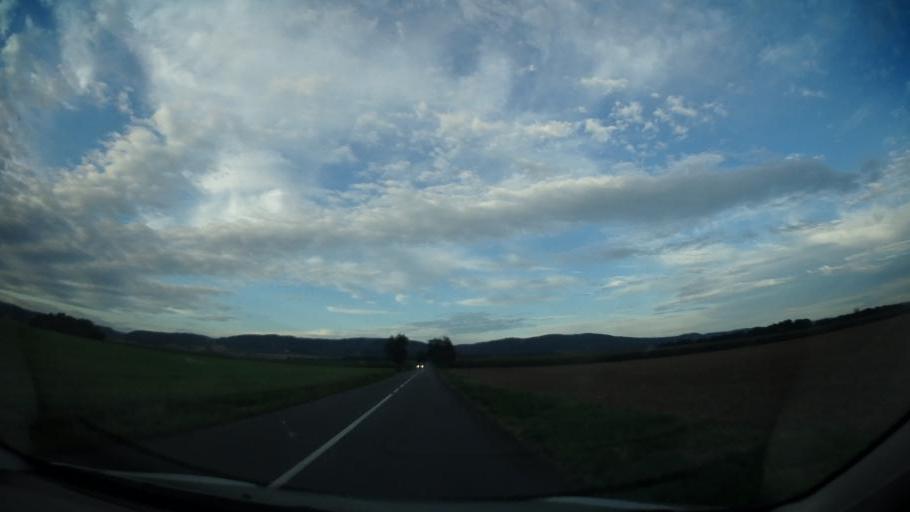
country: CZ
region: Olomoucky
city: Ujezd
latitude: 49.7824
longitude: 17.1755
